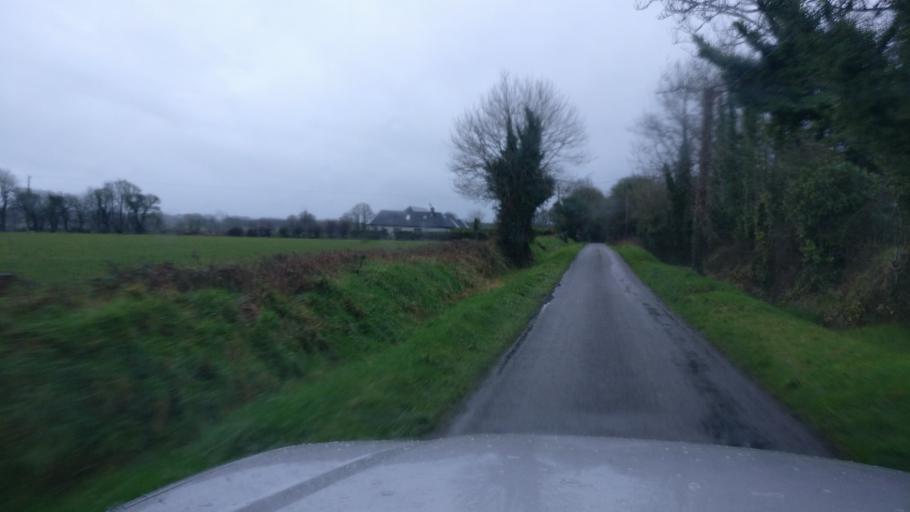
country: IE
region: Connaught
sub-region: County Galway
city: Loughrea
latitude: 53.2576
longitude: -8.3931
